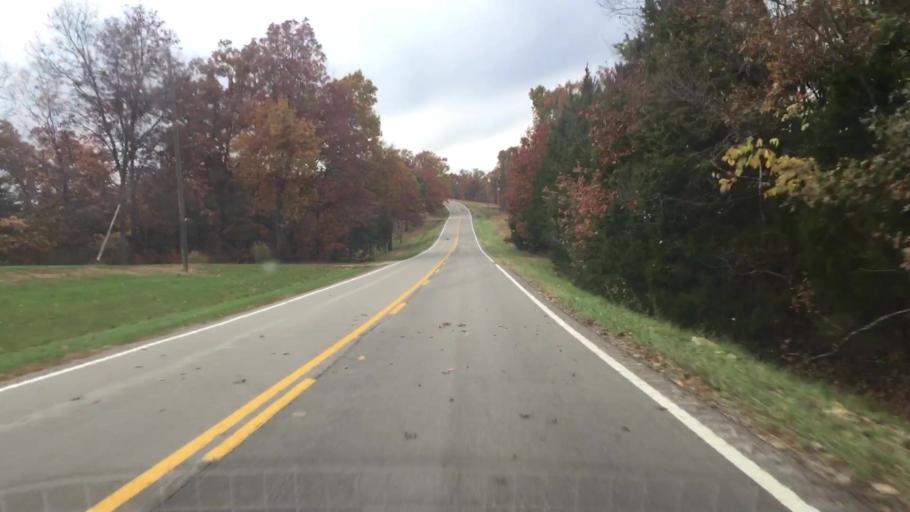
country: US
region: Missouri
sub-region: Gasconade County
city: Hermann
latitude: 38.7110
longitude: -91.6346
